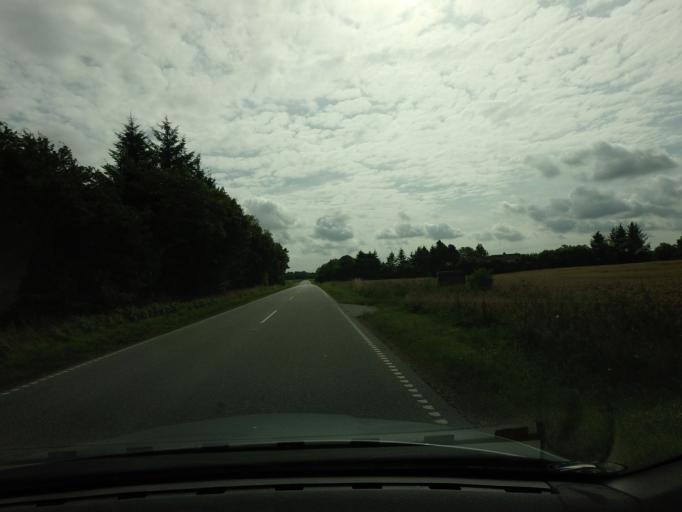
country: DK
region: North Denmark
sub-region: Bronderslev Kommune
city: Dronninglund
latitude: 57.2815
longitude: 10.2597
